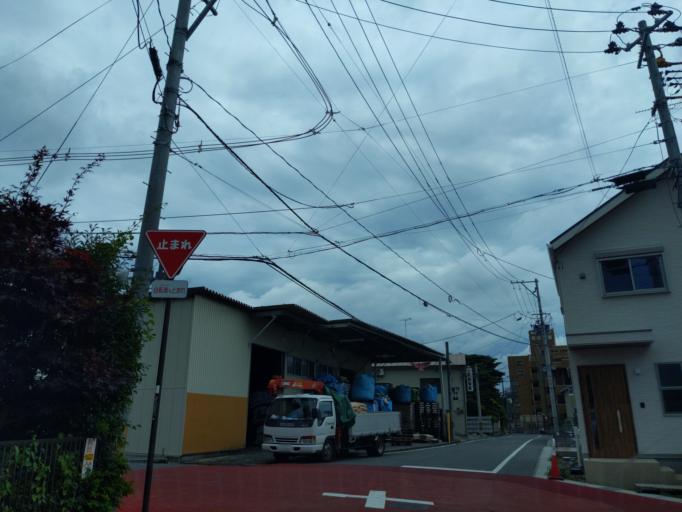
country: JP
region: Fukushima
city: Koriyama
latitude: 37.3878
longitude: 140.3743
